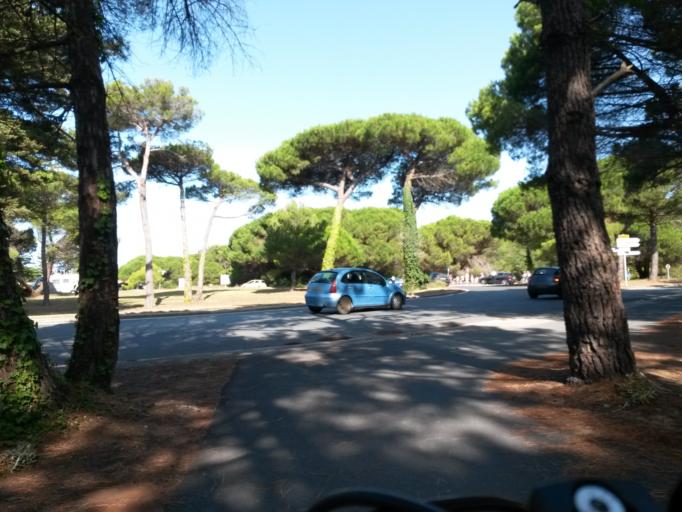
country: FR
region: Poitou-Charentes
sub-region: Departement de la Charente-Maritime
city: Le Bois-Plage-en-Re
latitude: 46.1788
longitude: -1.3737
